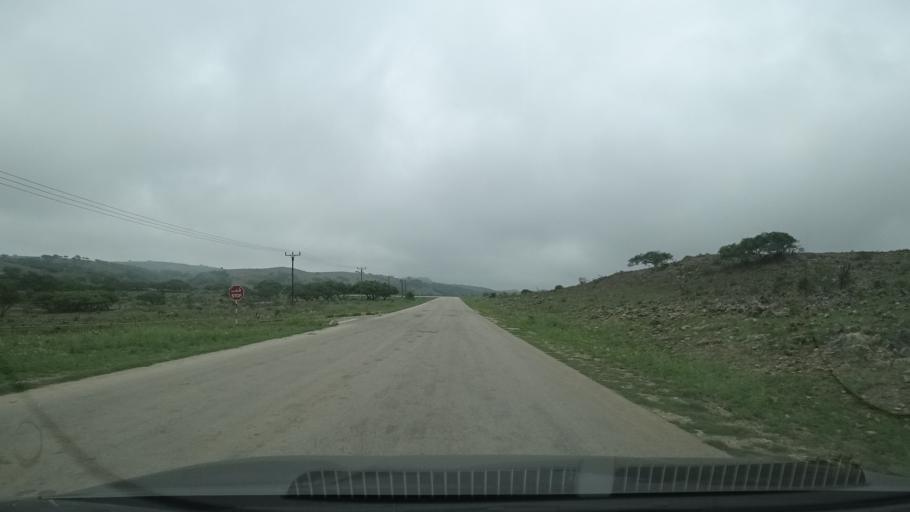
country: OM
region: Zufar
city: Salalah
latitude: 17.1181
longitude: 54.5712
